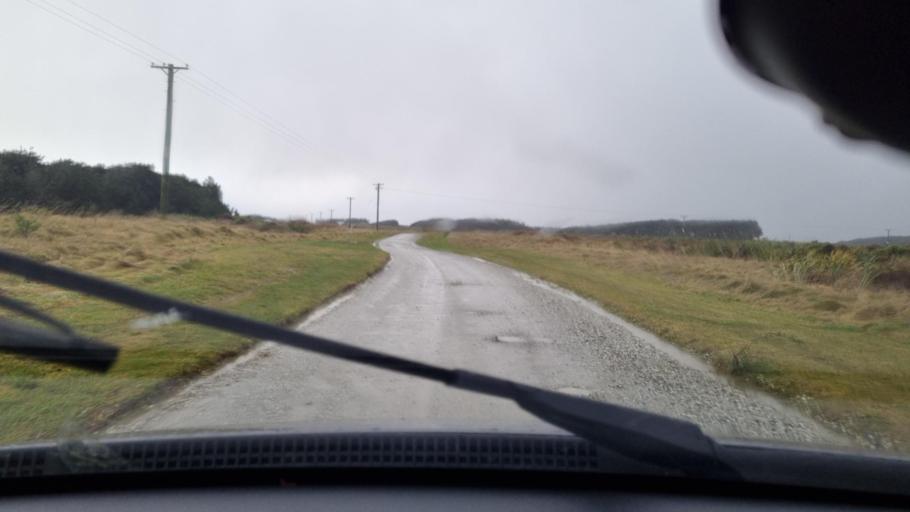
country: NZ
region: Southland
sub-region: Invercargill City
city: Invercargill
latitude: -46.4363
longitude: 168.2381
